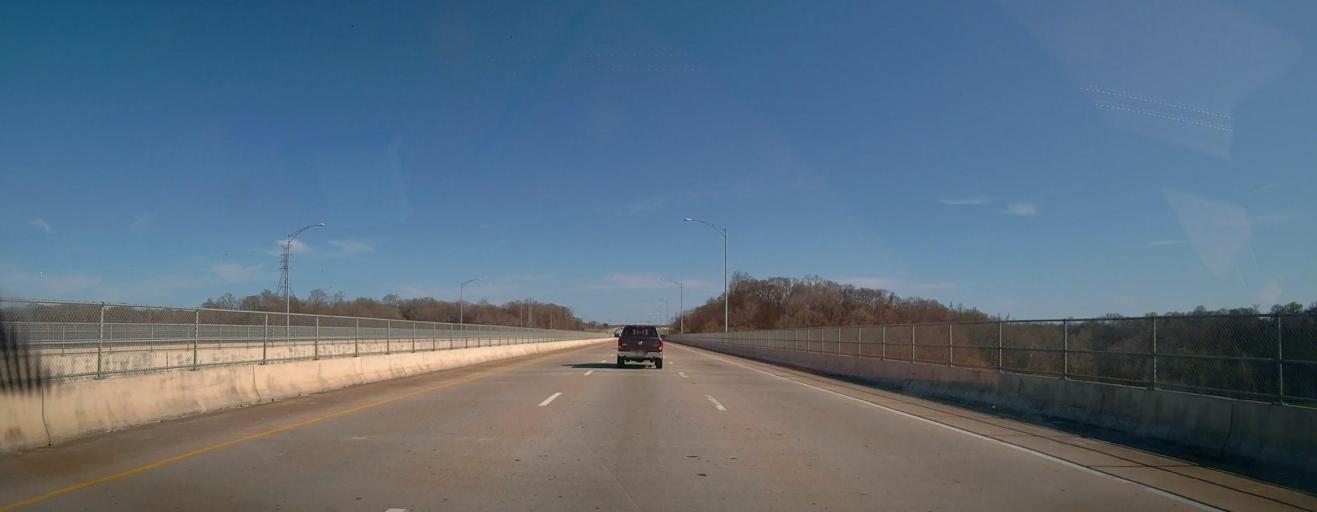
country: US
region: Alabama
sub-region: Lauderdale County
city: East Florence
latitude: 34.7933
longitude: -87.6442
